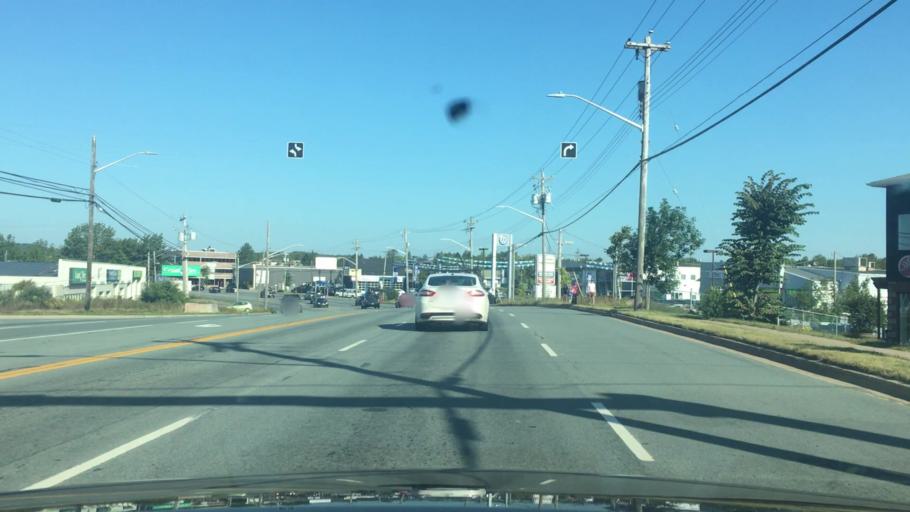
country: CA
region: Nova Scotia
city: Dartmouth
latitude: 44.7010
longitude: -63.6071
